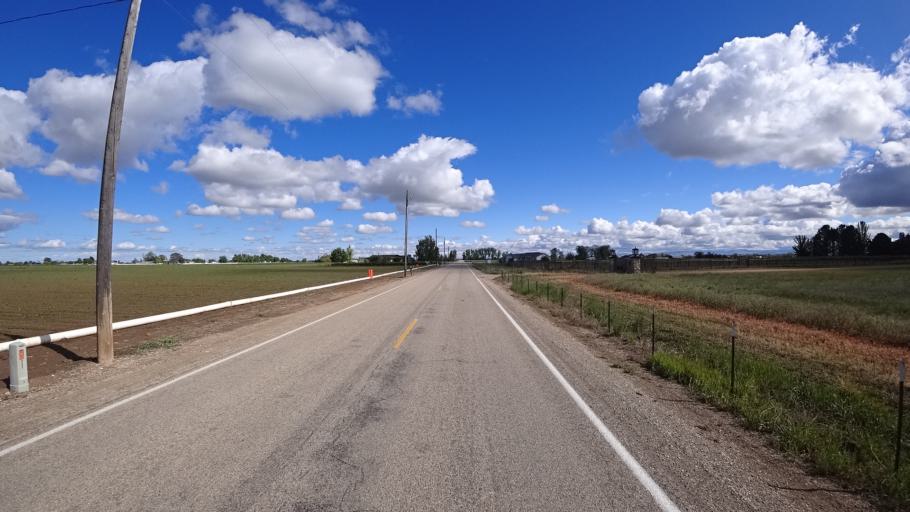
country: US
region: Idaho
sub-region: Ada County
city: Kuna
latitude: 43.5051
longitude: -116.4736
